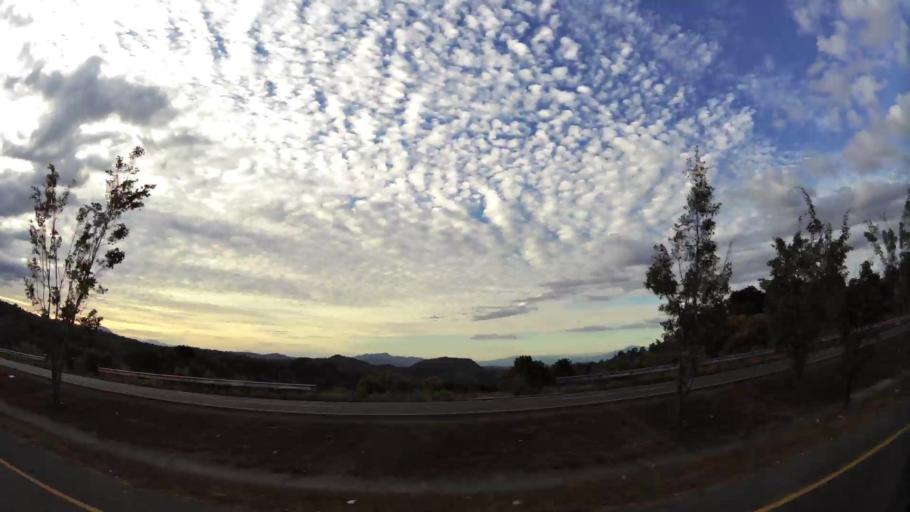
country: SV
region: Cuscatlan
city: Cojutepeque
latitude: 13.7251
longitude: -88.9008
